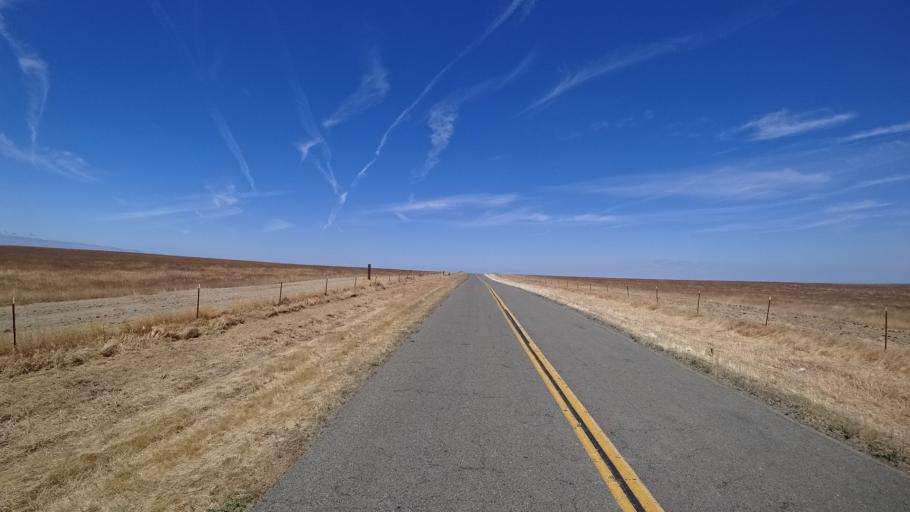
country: US
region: California
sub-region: Kings County
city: Kettleman City
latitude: 35.8003
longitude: -119.8952
